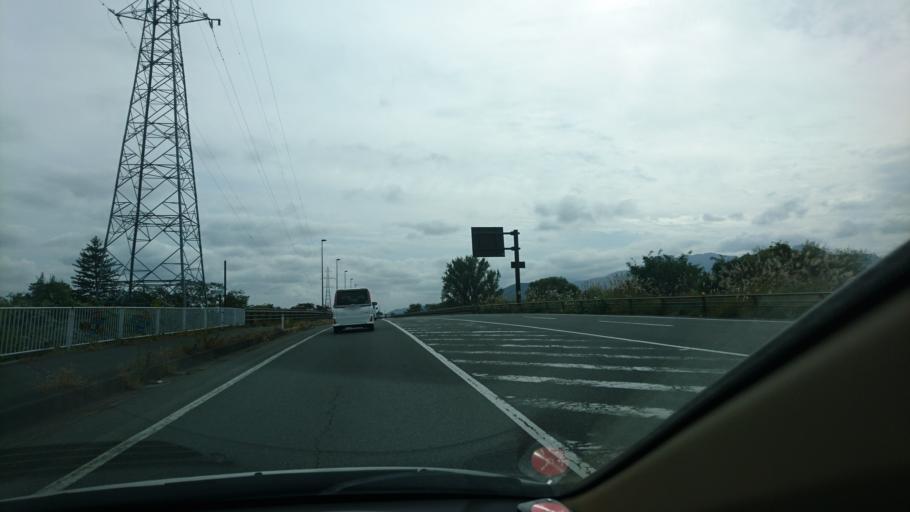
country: JP
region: Iwate
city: Morioka-shi
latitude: 39.7089
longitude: 141.1015
